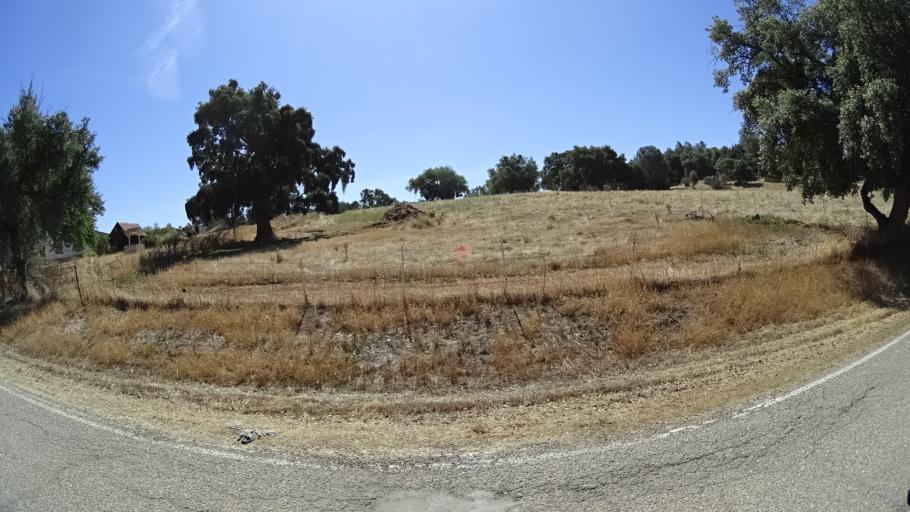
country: US
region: California
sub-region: Calaveras County
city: Valley Springs
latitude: 38.2244
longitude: -120.8555
